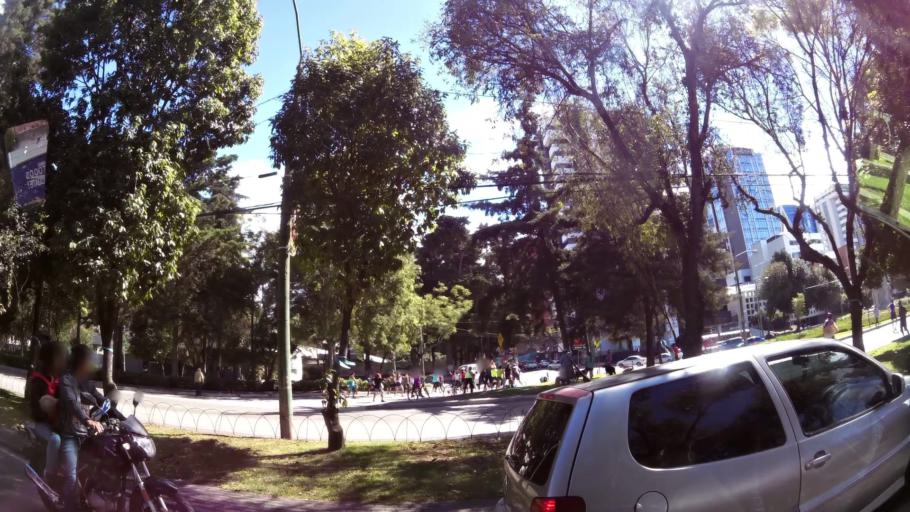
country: GT
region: Guatemala
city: Santa Catarina Pinula
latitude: 14.6013
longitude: -90.5167
